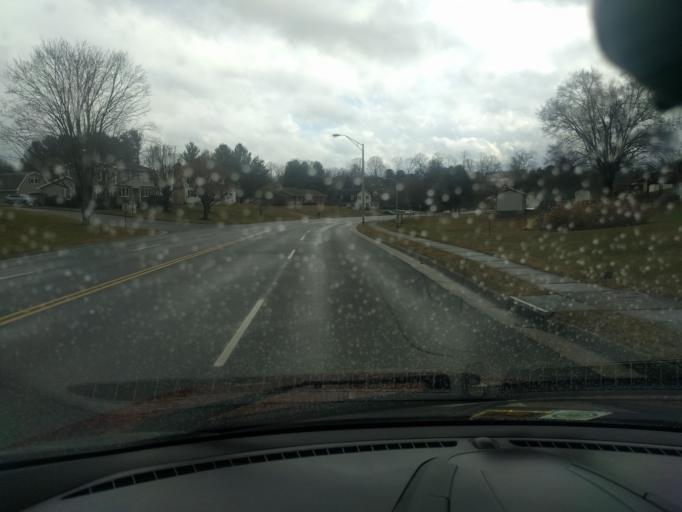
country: US
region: Virginia
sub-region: Pulaski County
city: Pulaski
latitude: 37.0604
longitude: -80.7577
